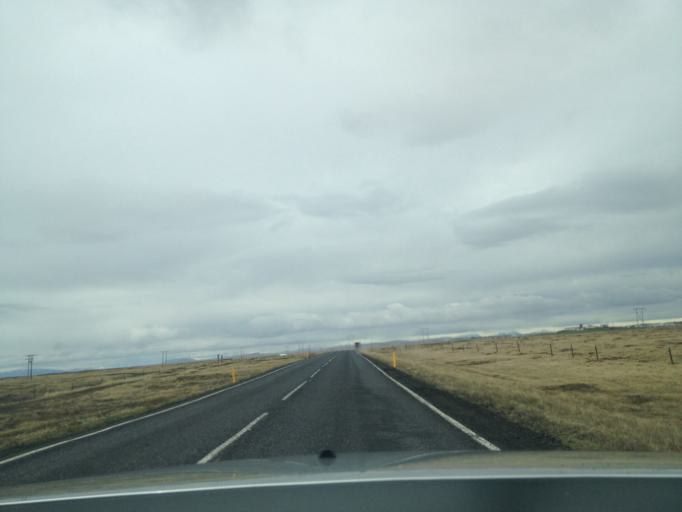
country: IS
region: South
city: Vestmannaeyjar
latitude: 63.7155
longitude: -20.2286
